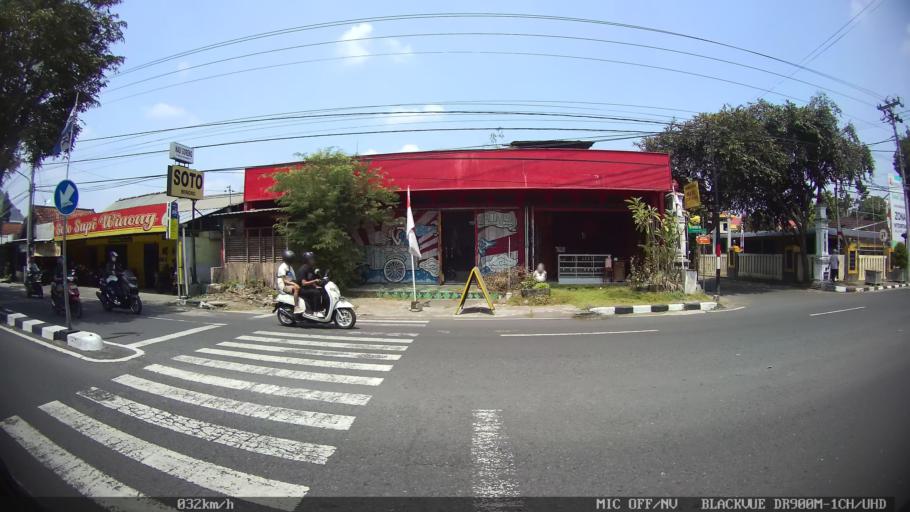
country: ID
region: Daerah Istimewa Yogyakarta
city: Yogyakarta
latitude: -7.8191
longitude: 110.3953
